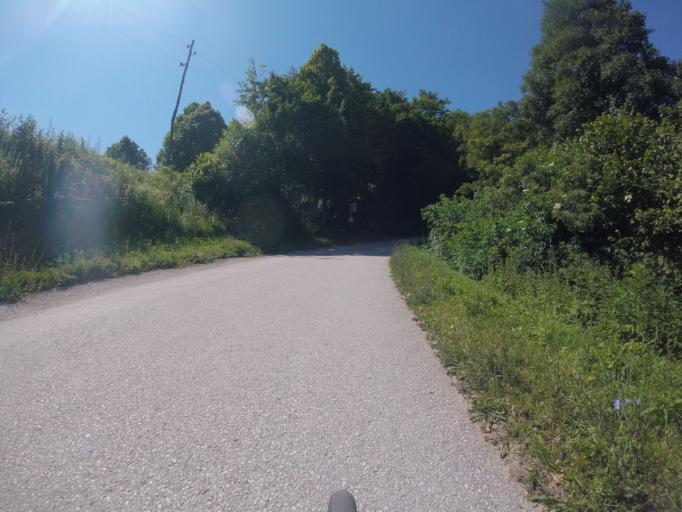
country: SI
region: Kostanjevica na Krki
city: Kostanjevica na Krki
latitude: 45.8043
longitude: 15.4983
